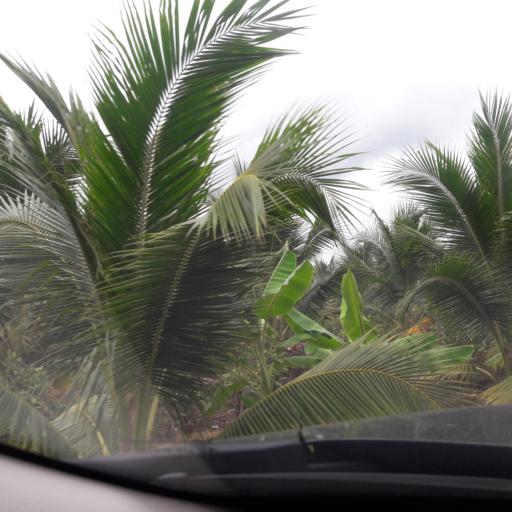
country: TH
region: Ratchaburi
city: Damnoen Saduak
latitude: 13.5773
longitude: 99.9486
